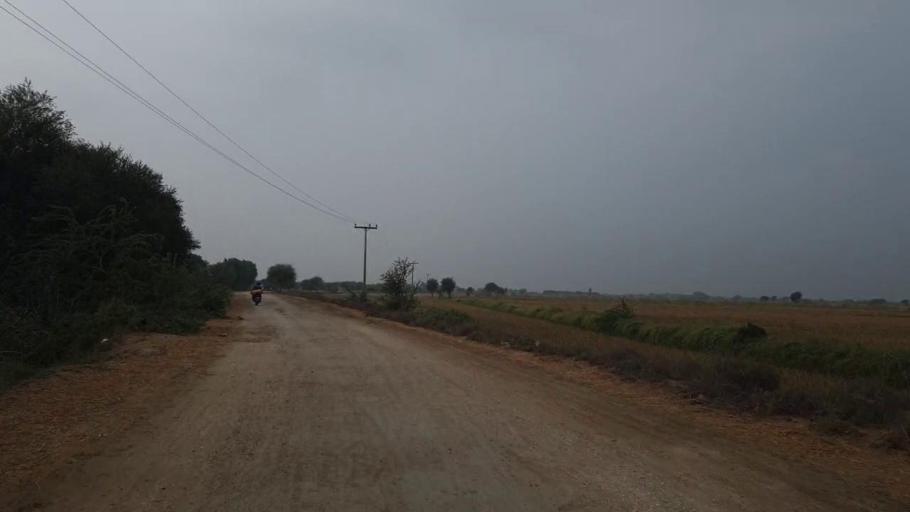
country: PK
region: Sindh
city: Kario
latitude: 24.9341
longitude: 68.5747
